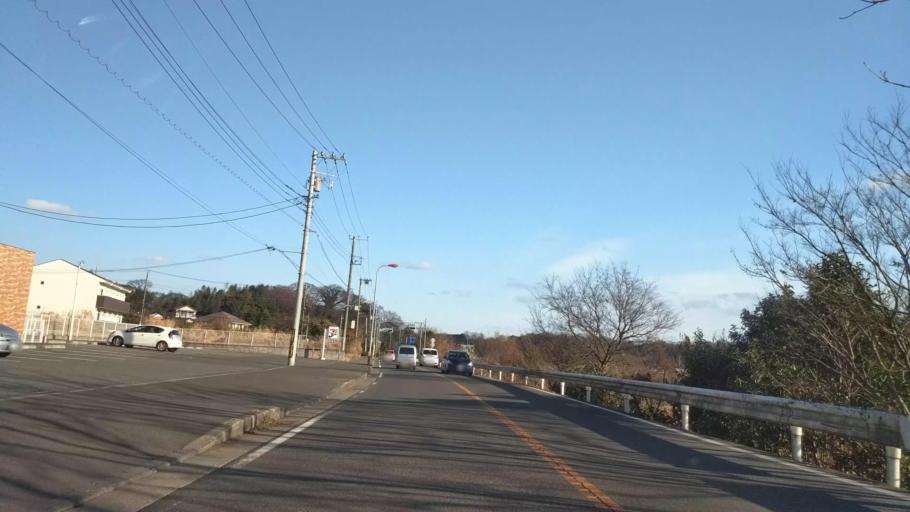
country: JP
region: Kanagawa
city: Hadano
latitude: 35.3572
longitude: 139.2659
